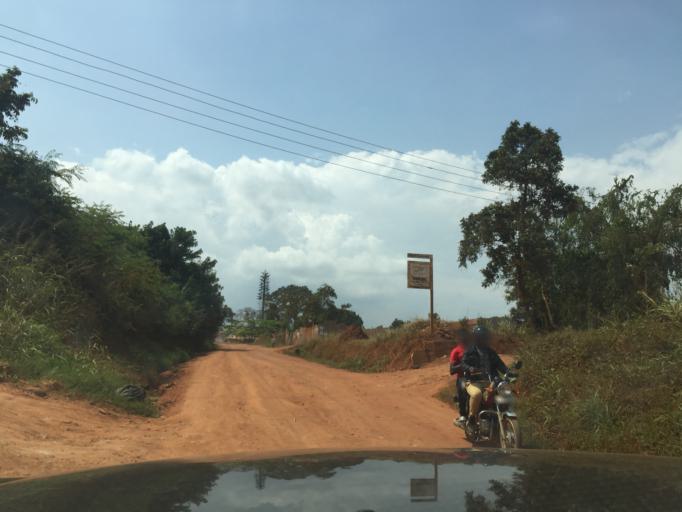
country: UG
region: Central Region
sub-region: Wakiso District
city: Kireka
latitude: 0.3971
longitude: 32.6228
